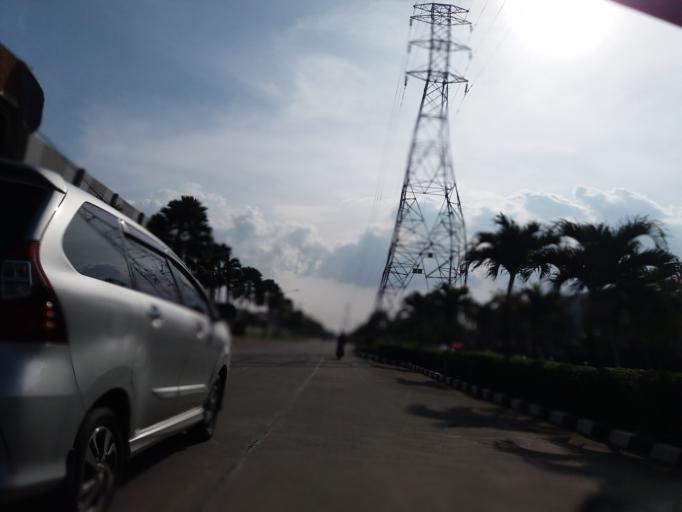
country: ID
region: West Java
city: Bandung
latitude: -6.9557
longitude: 107.6355
